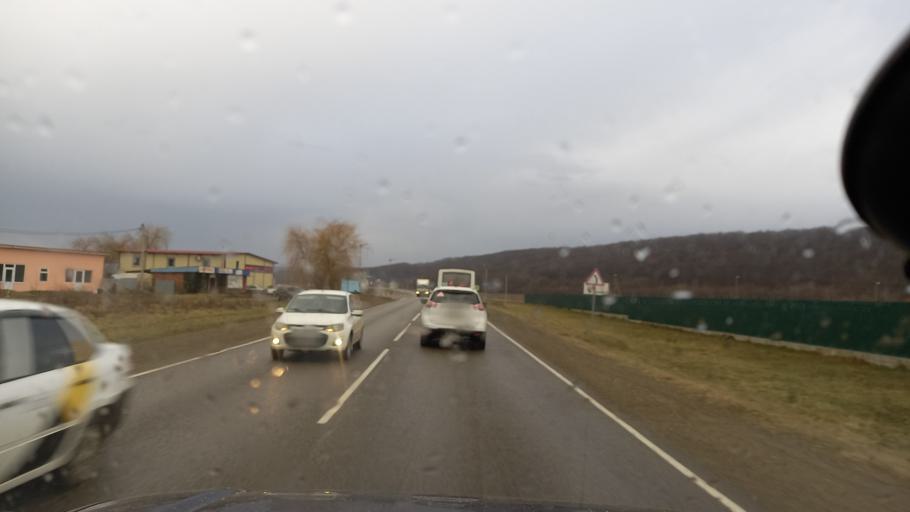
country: RU
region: Adygeya
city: Tul'skiy
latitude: 44.5274
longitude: 40.1363
